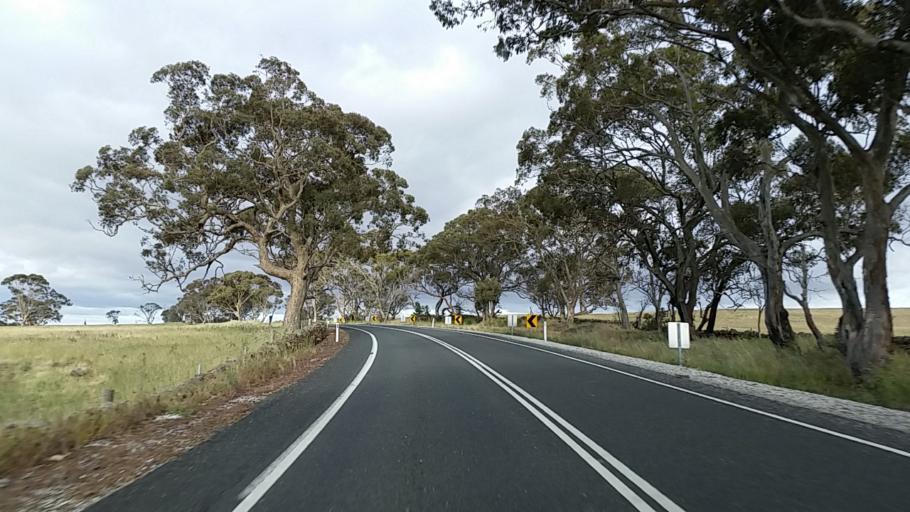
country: AU
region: South Australia
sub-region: Barossa
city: Angaston
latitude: -34.5640
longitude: 139.1840
